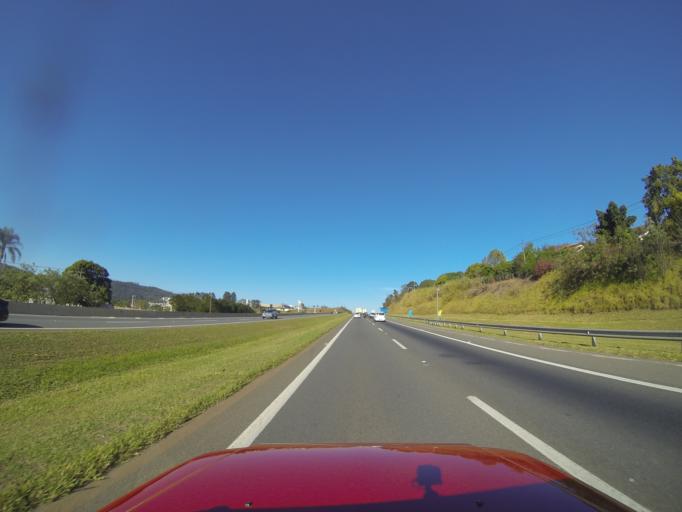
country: BR
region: Sao Paulo
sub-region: Bom Jesus Dos Perdoes
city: Bom Jesus dos Perdoes
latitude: -23.1119
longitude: -46.5038
